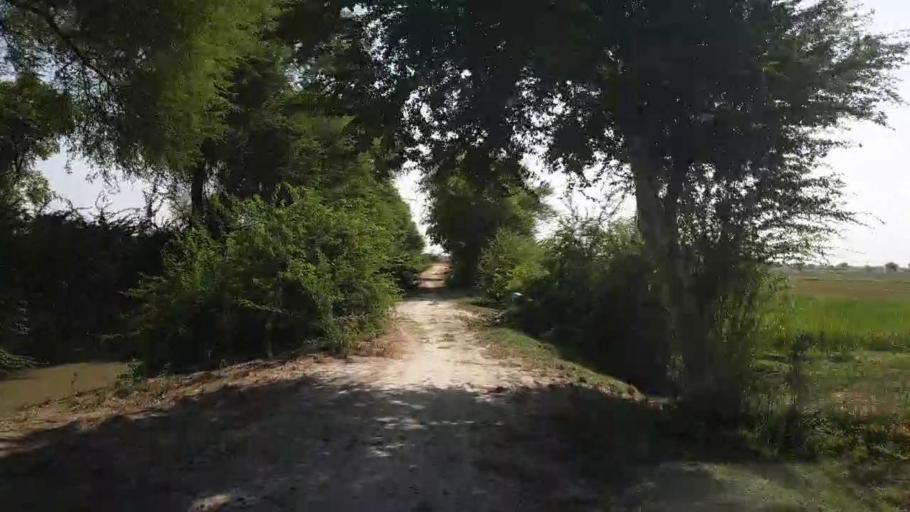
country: PK
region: Sindh
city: Kadhan
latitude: 24.6257
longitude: 68.9944
